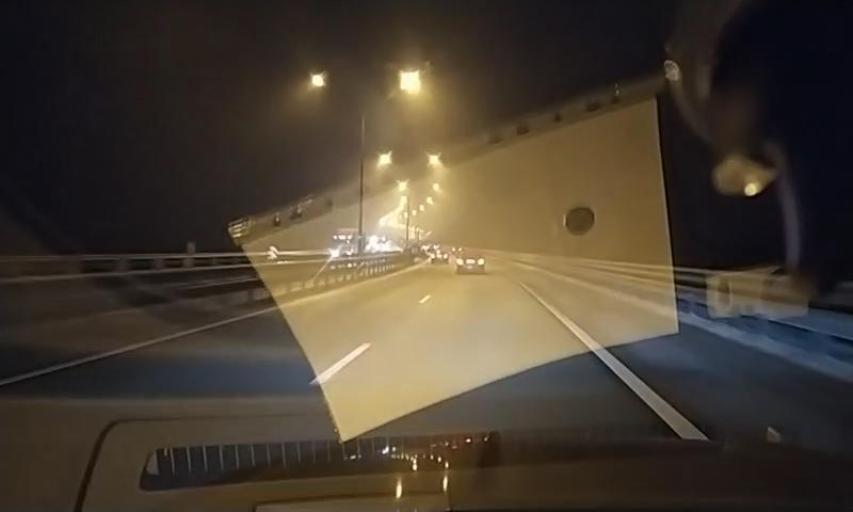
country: RU
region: Leningrad
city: Bugry
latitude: 60.1092
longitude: 30.3875
